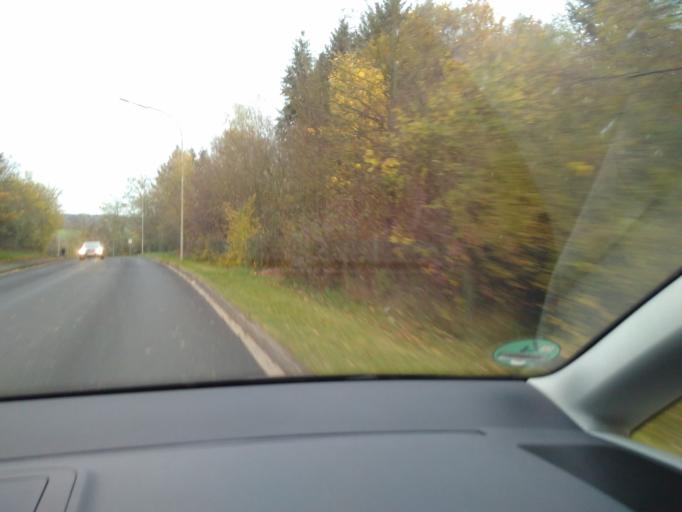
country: DE
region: Hesse
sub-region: Regierungsbezirk Giessen
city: Lauterbach
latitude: 50.6428
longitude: 9.3834
